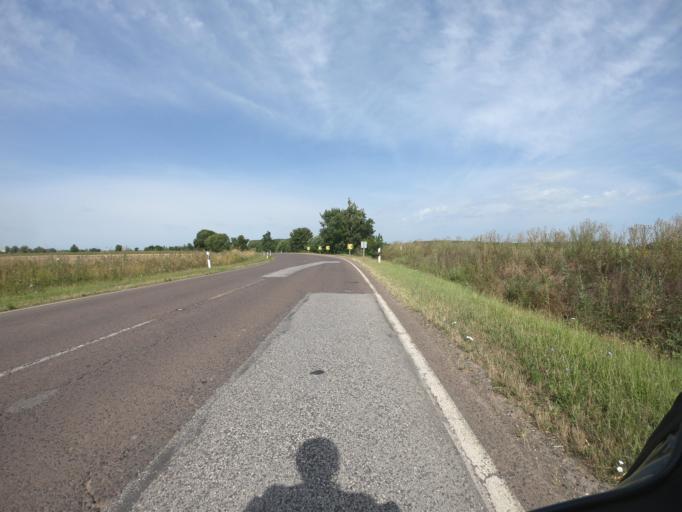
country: HU
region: Jasz-Nagykun-Szolnok
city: Tiszafured
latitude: 47.5975
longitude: 20.8234
